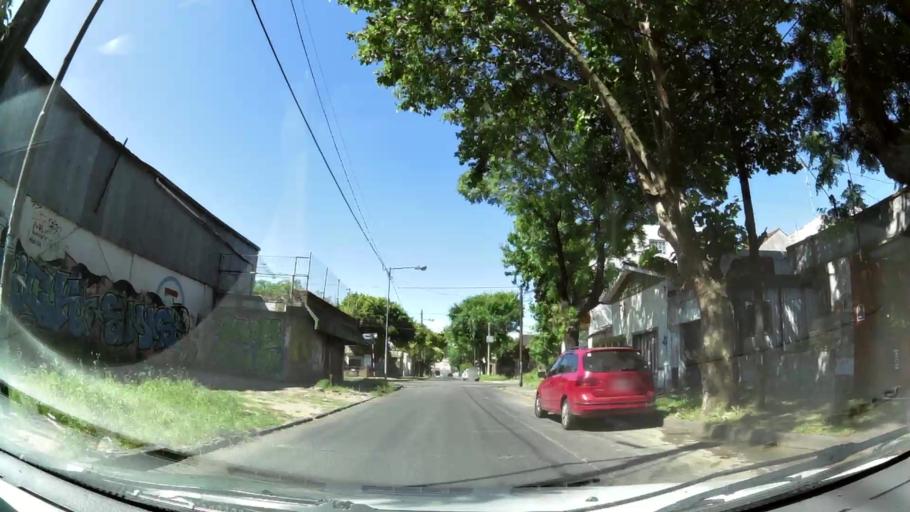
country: AR
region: Buenos Aires
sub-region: Partido de General San Martin
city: General San Martin
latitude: -34.5488
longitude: -58.5636
